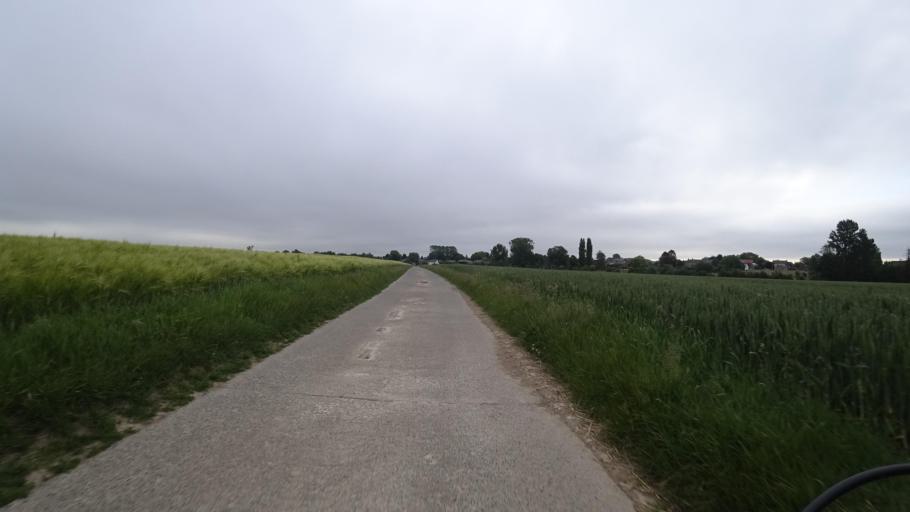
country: BE
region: Wallonia
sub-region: Province de Namur
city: Gembloux
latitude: 50.5316
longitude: 4.7725
